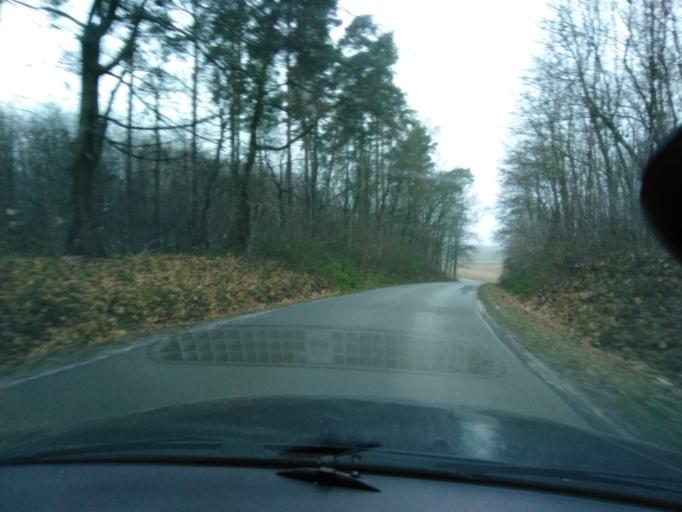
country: PL
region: Subcarpathian Voivodeship
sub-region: Powiat przeworski
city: Zurawiczki
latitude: 49.9993
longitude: 22.5063
